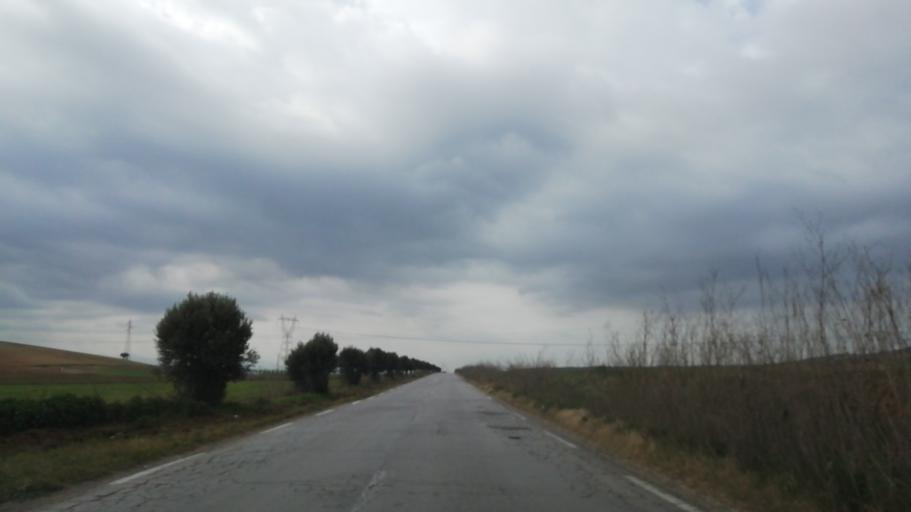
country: DZ
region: Oran
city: Sidi ech Chahmi
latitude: 35.6263
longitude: -0.4045
